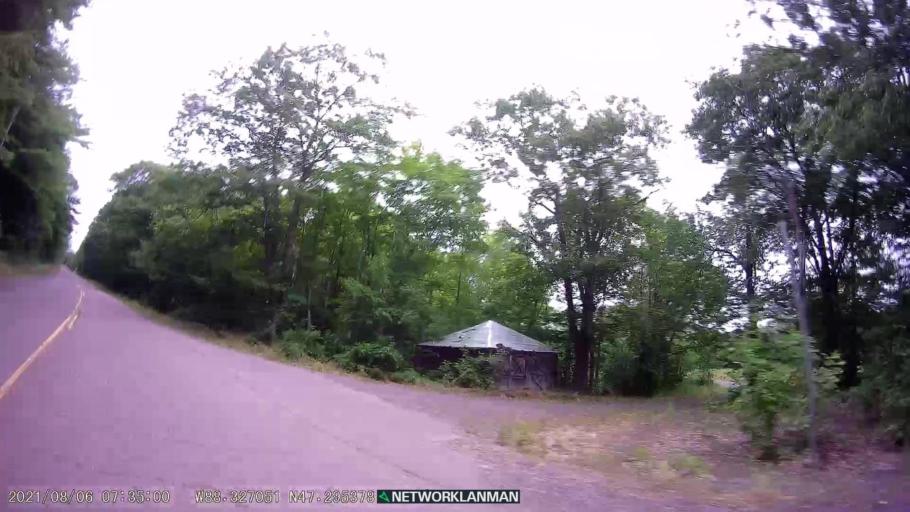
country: US
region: Michigan
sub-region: Keweenaw County
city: Eagle River
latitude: 47.2958
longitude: -88.3276
